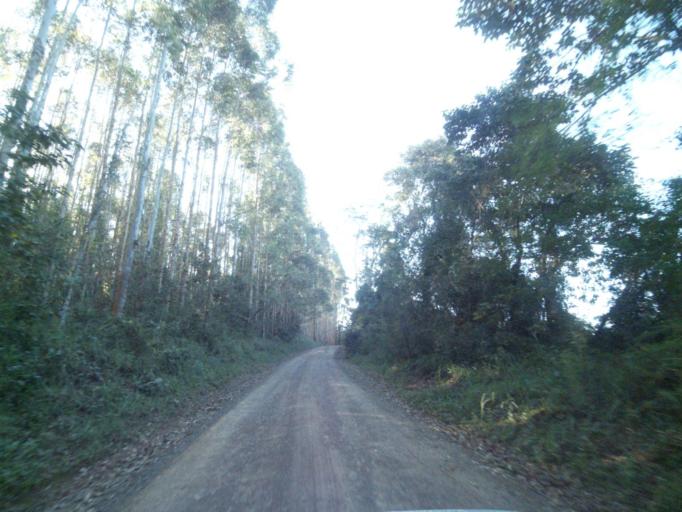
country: BR
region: Parana
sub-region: Telemaco Borba
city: Telemaco Borba
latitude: -24.5035
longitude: -50.5981
